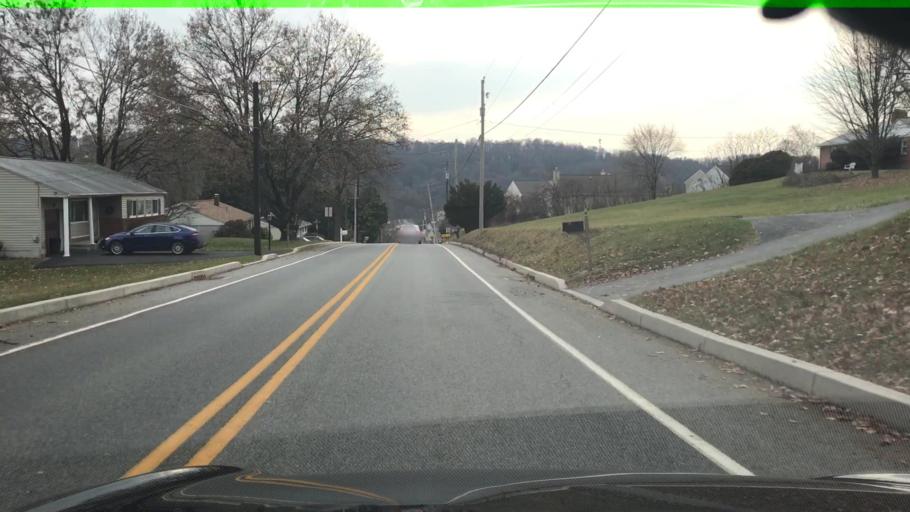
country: US
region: Pennsylvania
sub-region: Dauphin County
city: Steelton
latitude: 40.1893
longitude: -76.8592
